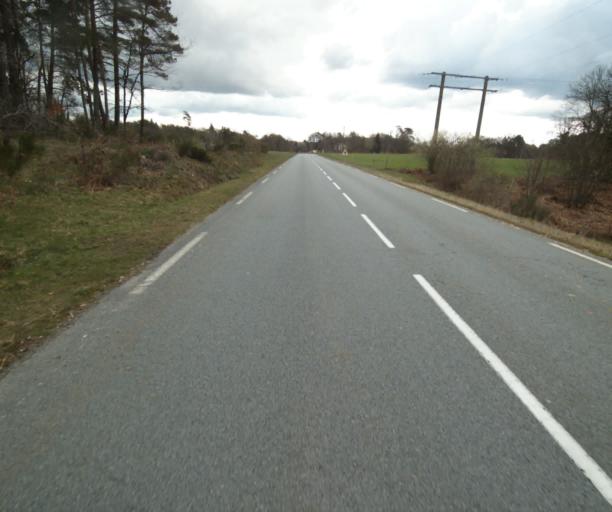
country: FR
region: Limousin
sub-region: Departement de la Correze
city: Correze
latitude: 45.2854
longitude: 1.9062
